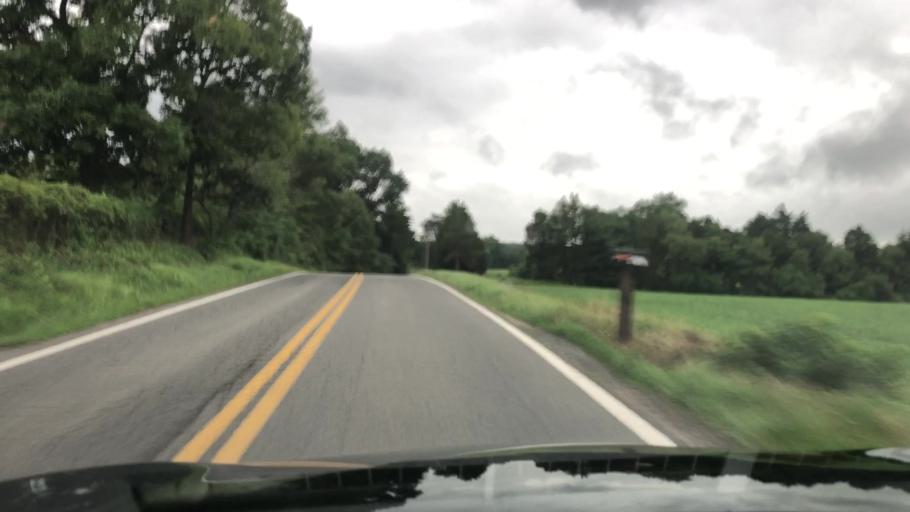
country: US
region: Virginia
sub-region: Prince William County
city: Nokesville
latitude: 38.5950
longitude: -77.6016
